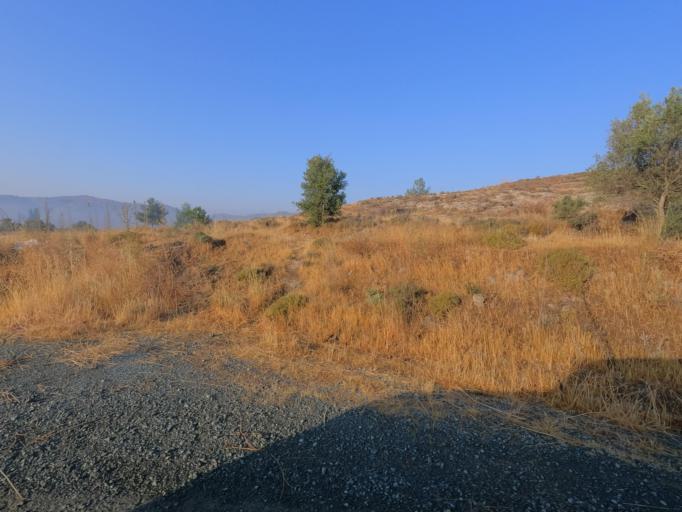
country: CY
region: Larnaka
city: Mosfiloti
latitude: 34.9731
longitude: 33.4388
